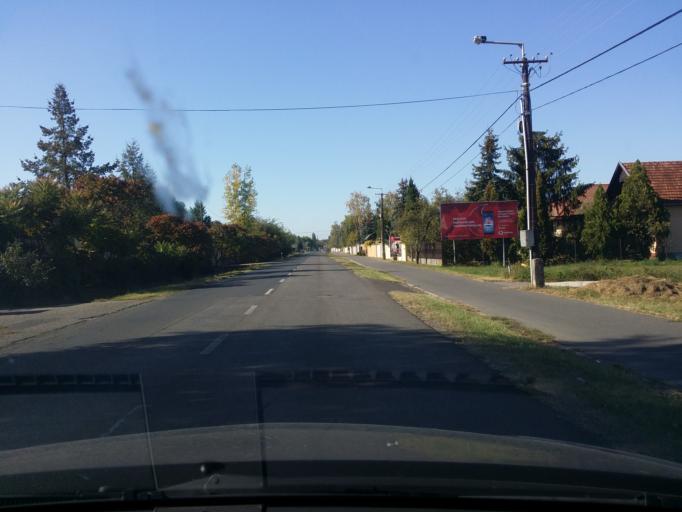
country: HU
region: Bekes
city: Bekescsaba
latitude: 46.6891
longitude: 21.1203
